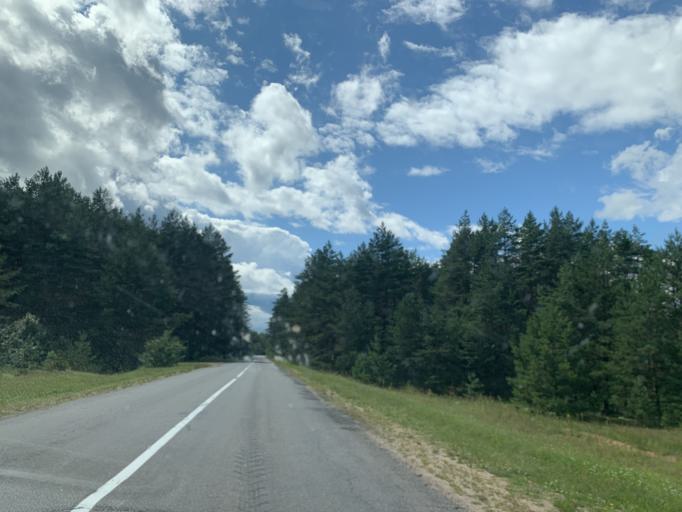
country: BY
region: Minsk
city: Rakaw
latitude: 53.9868
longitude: 26.9426
